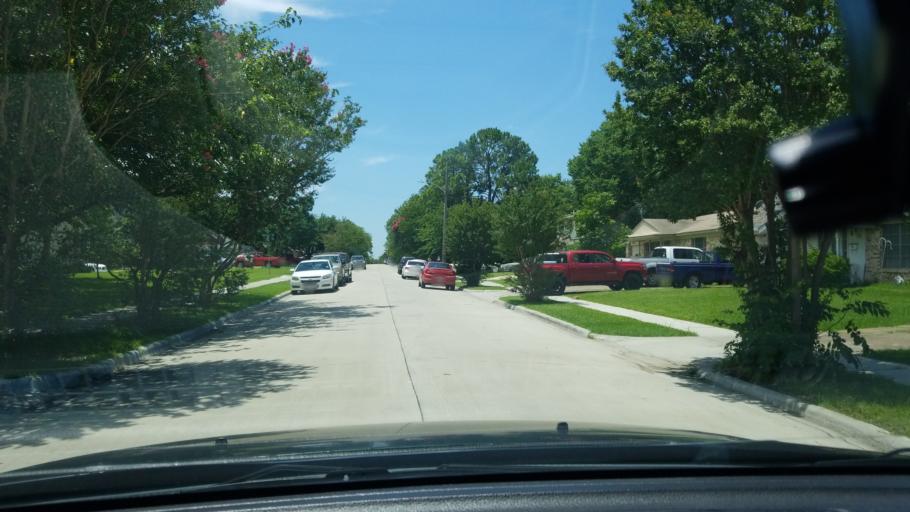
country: US
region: Texas
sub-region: Dallas County
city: Mesquite
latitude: 32.8036
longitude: -96.6515
